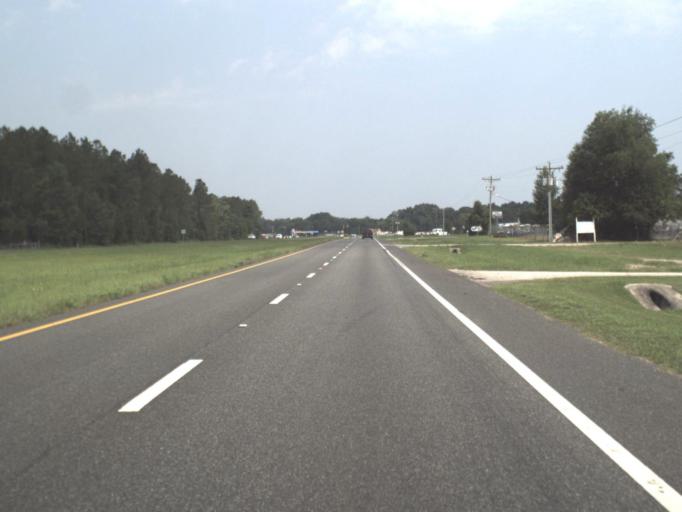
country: US
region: Florida
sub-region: Levy County
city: Williston
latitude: 29.3826
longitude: -82.4239
